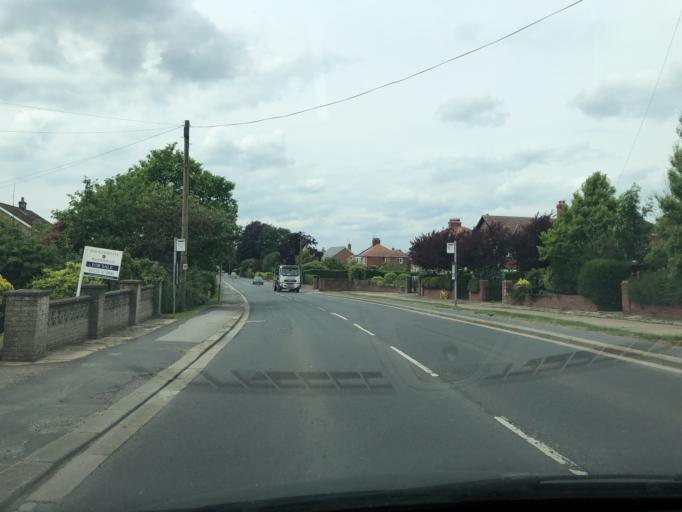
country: GB
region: England
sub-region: North Yorkshire
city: Pickering
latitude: 54.2397
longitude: -0.7621
